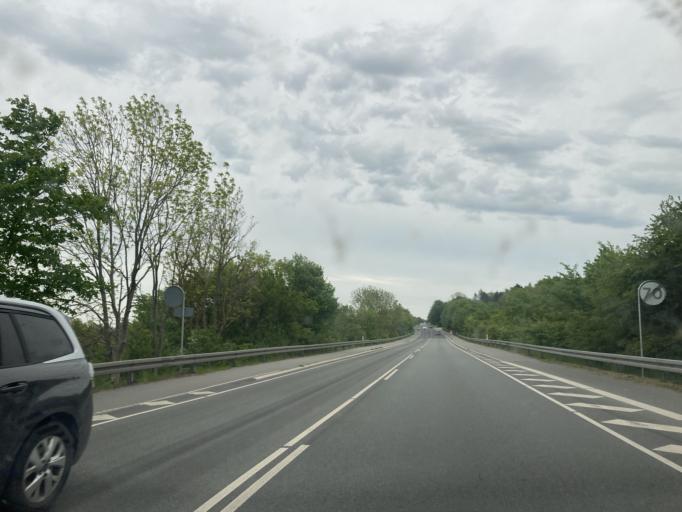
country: DK
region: Zealand
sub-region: Roskilde Kommune
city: Svogerslev
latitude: 55.6342
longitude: 11.9919
